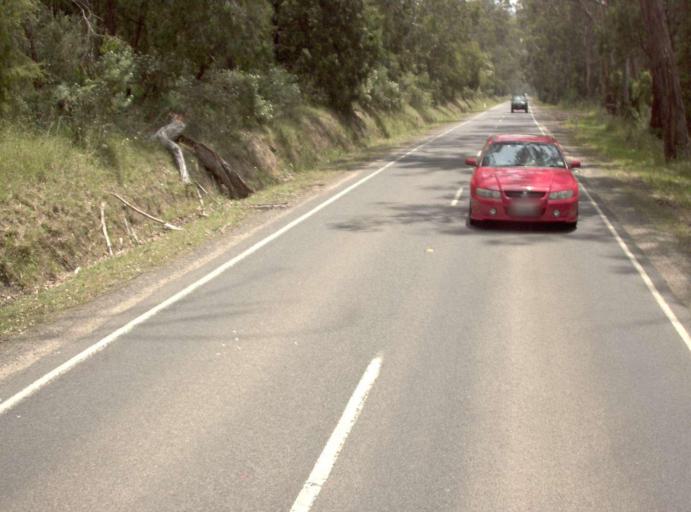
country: AU
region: Victoria
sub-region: Latrobe
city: Traralgon
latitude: -38.4023
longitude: 146.7497
